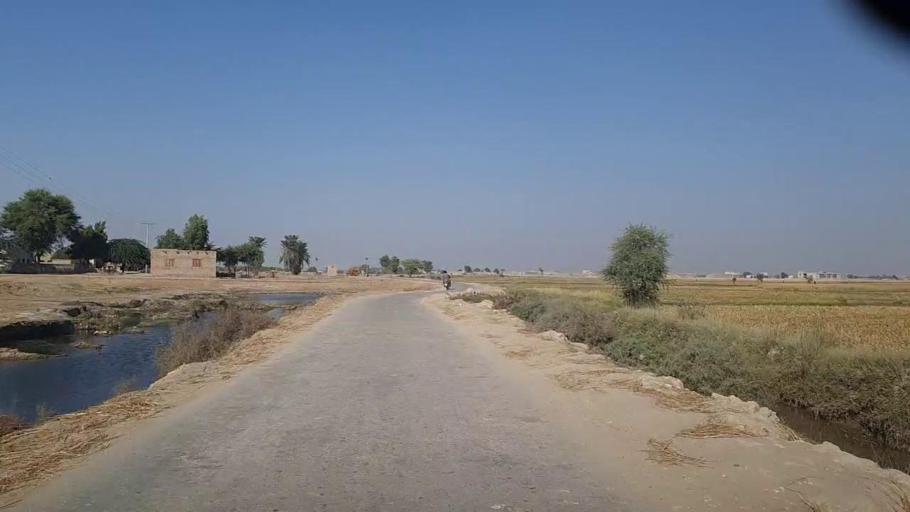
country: PK
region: Sindh
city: Tangwani
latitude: 28.2545
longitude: 68.9961
